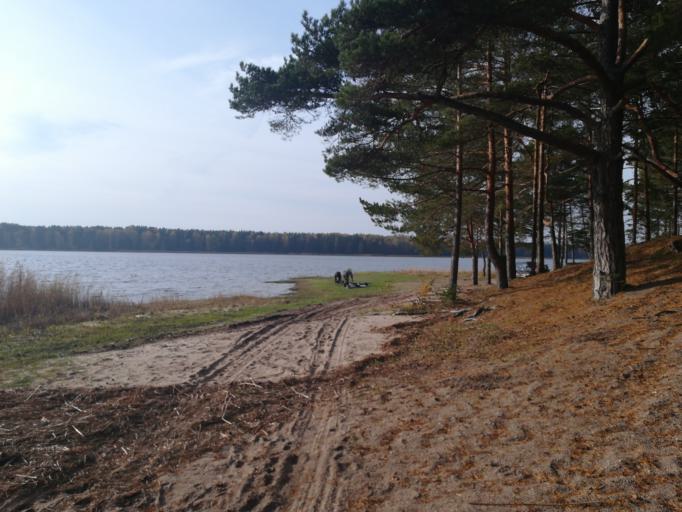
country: RU
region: Leningrad
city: Ust'-Luga
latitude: 59.7508
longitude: 28.1513
